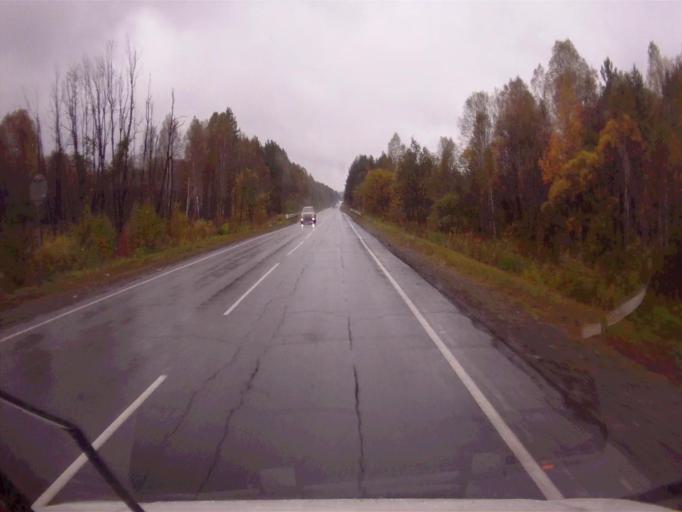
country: RU
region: Chelyabinsk
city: Verkhniy Ufaley
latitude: 55.9727
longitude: 60.3555
